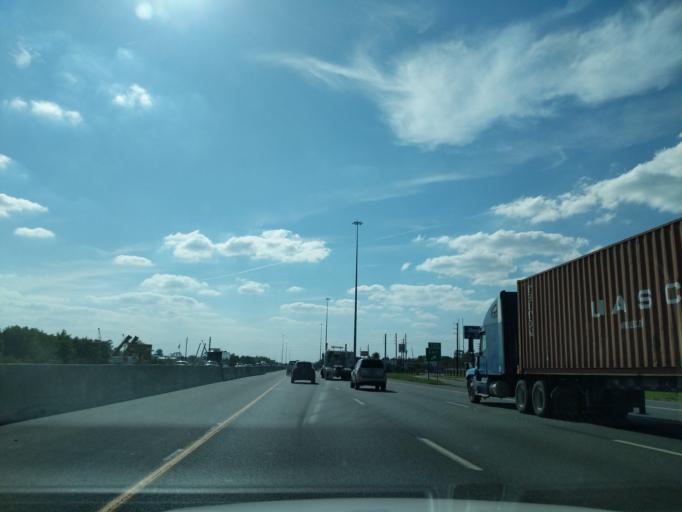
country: US
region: Texas
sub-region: Harris County
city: Channelview
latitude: 29.7889
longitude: -95.0926
